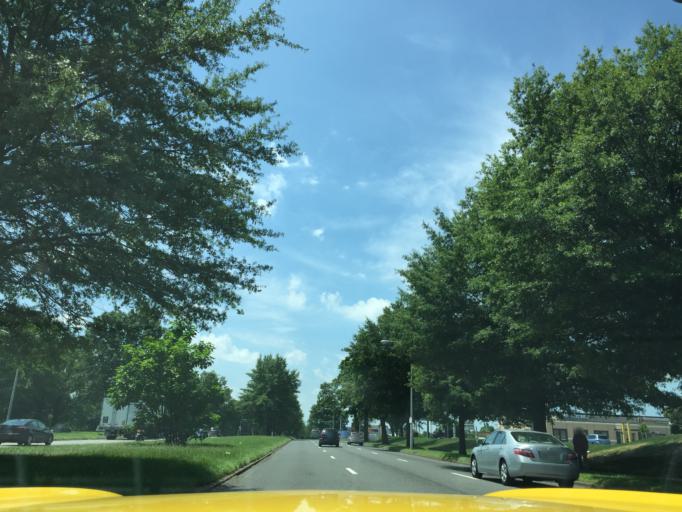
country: US
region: Pennsylvania
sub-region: Bucks County
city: Feasterville
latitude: 40.1015
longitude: -75.0066
